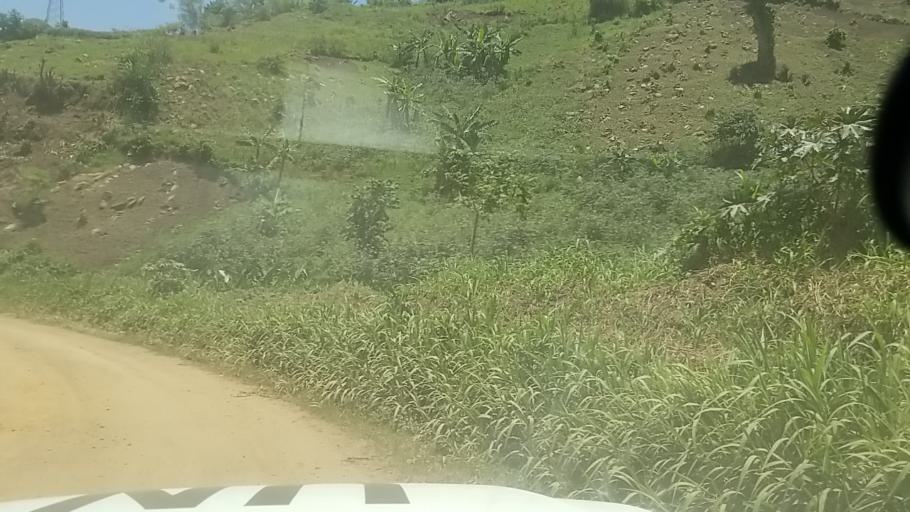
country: CD
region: Nord Kivu
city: Sake
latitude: -1.8395
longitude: 28.9969
